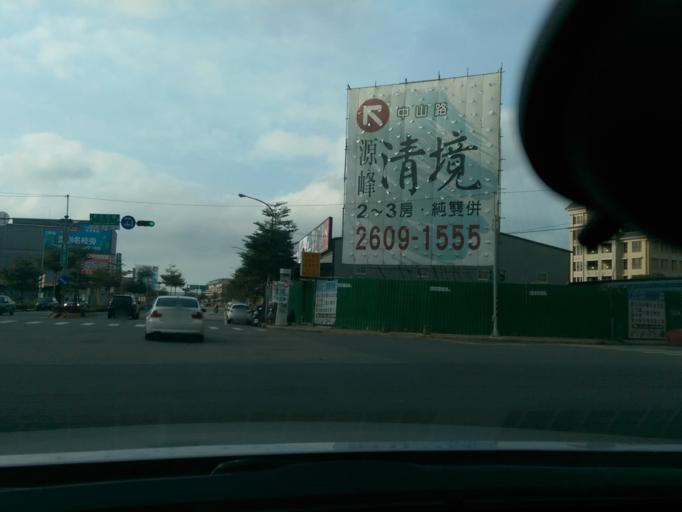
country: TW
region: Taiwan
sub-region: Taoyuan
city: Taoyuan
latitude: 25.0842
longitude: 121.3775
